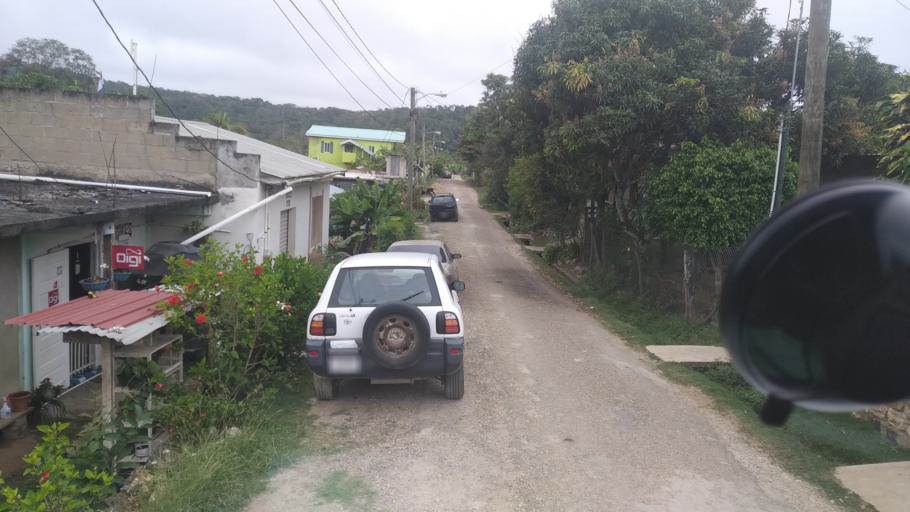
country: BZ
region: Cayo
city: Benque Viejo del Carmen
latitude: 17.0835
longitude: -89.1282
